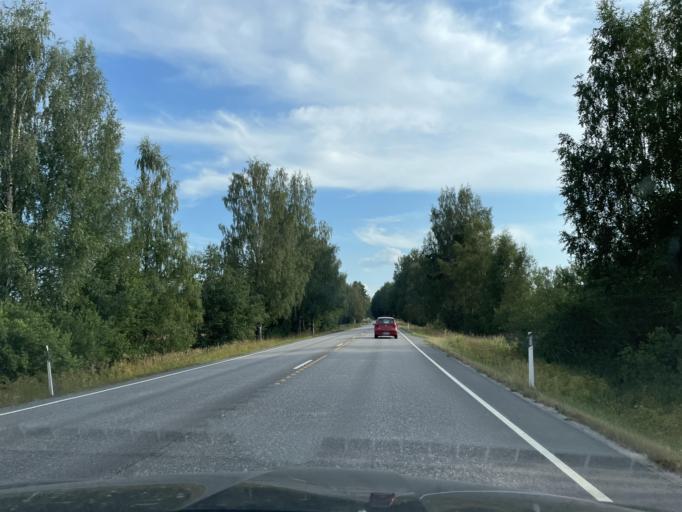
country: FI
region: Paijanne Tavastia
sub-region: Lahti
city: Padasjoki
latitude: 61.4239
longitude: 25.1838
